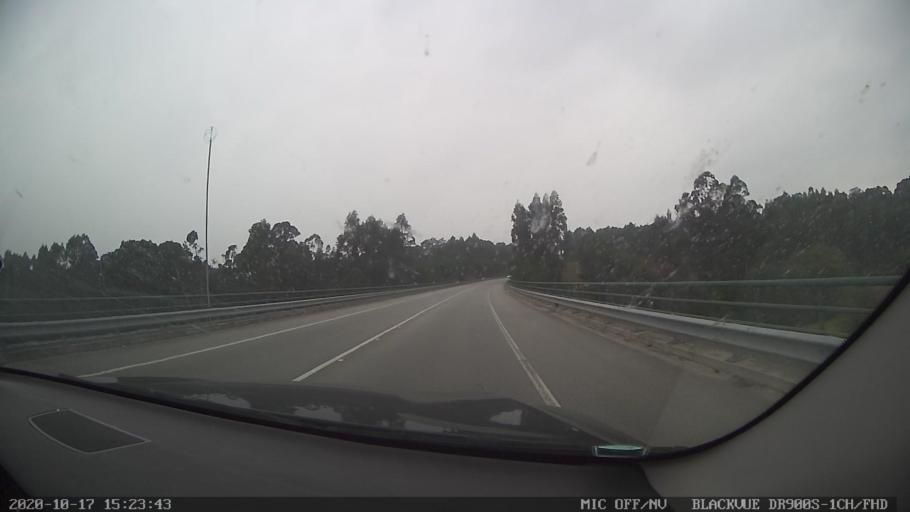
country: PT
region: Braga
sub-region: Esposende
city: Esposende
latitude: 41.5284
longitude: -8.7435
